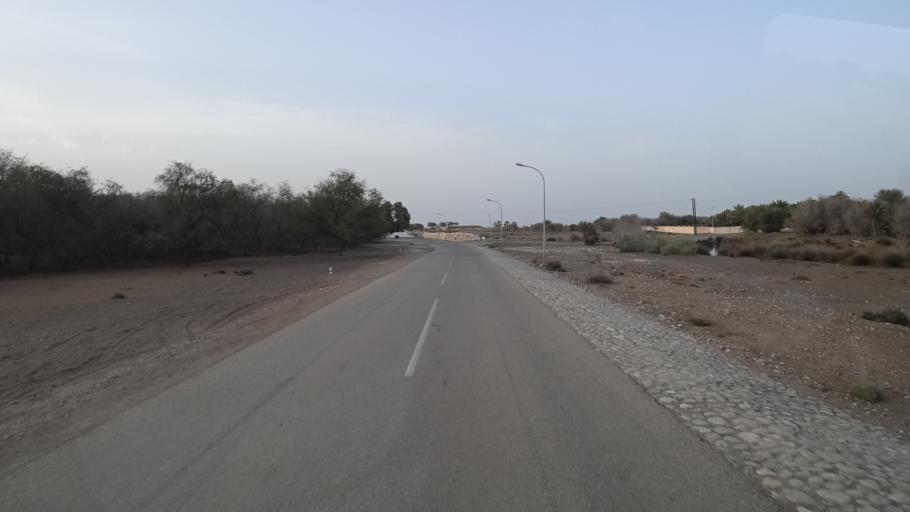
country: OM
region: Muhafazat Masqat
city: Muscat
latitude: 23.2113
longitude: 58.9736
